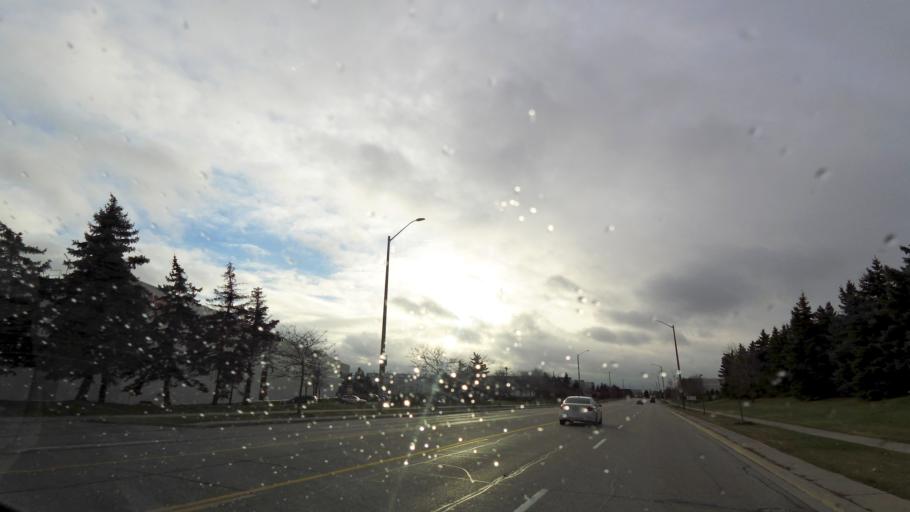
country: CA
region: Ontario
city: Mississauga
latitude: 43.6244
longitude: -79.6884
